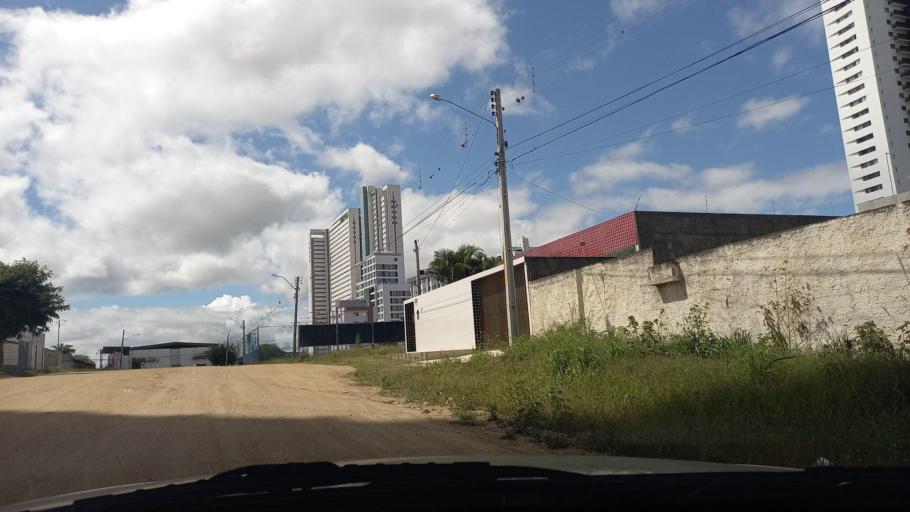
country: BR
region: Pernambuco
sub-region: Caruaru
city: Caruaru
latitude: -8.2641
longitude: -35.9674
